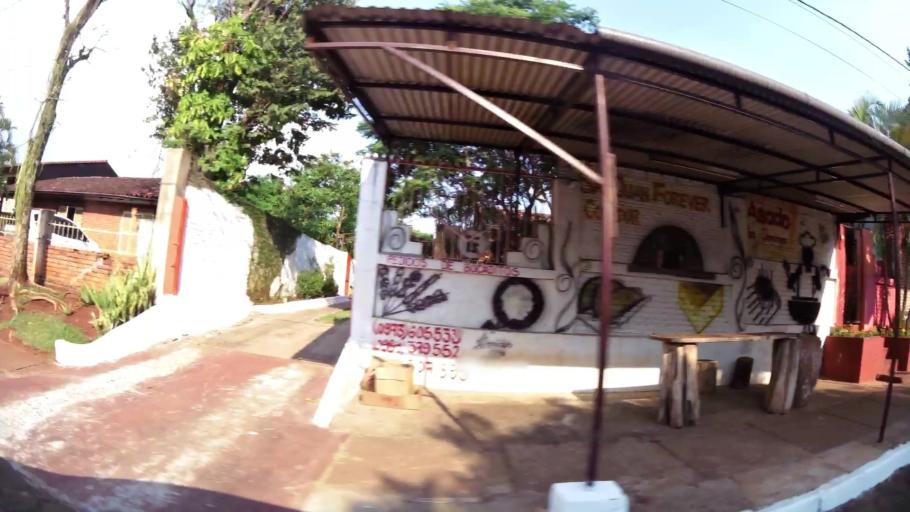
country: PY
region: Alto Parana
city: Presidente Franco
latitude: -25.5322
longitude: -54.6294
